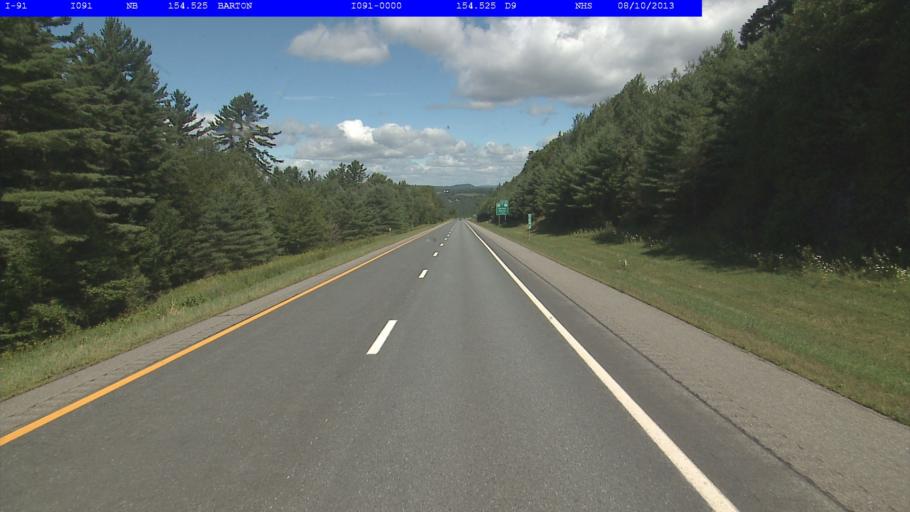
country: US
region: Vermont
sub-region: Orleans County
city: Newport
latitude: 44.7166
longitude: -72.1747
